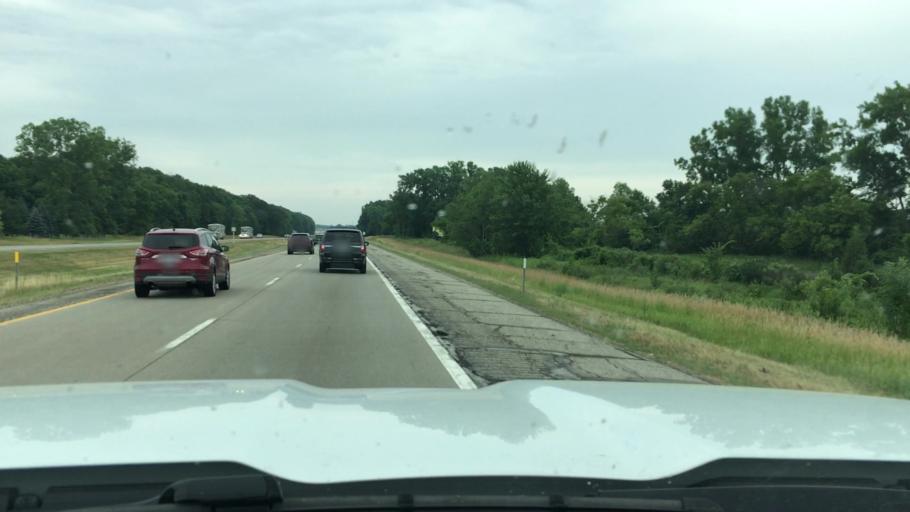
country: US
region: Michigan
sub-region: Eaton County
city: Grand Ledge
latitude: 42.8093
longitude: -84.7756
